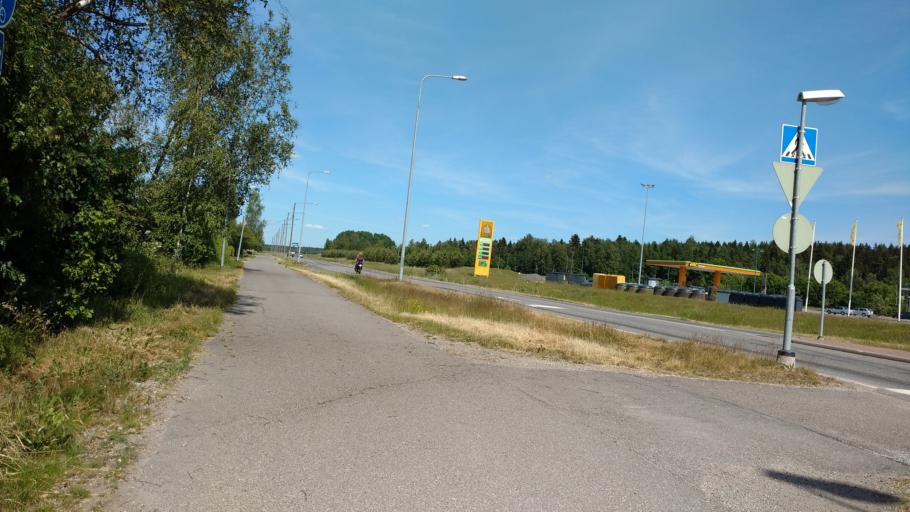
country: FI
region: Varsinais-Suomi
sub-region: Salo
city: Salo
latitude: 60.4040
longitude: 23.1680
